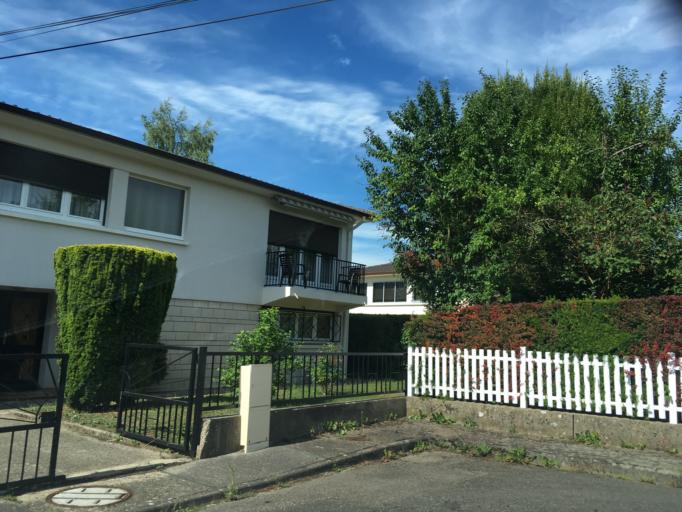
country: FR
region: Lorraine
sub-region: Departement de la Moselle
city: Marly
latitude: 49.0723
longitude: 6.1812
